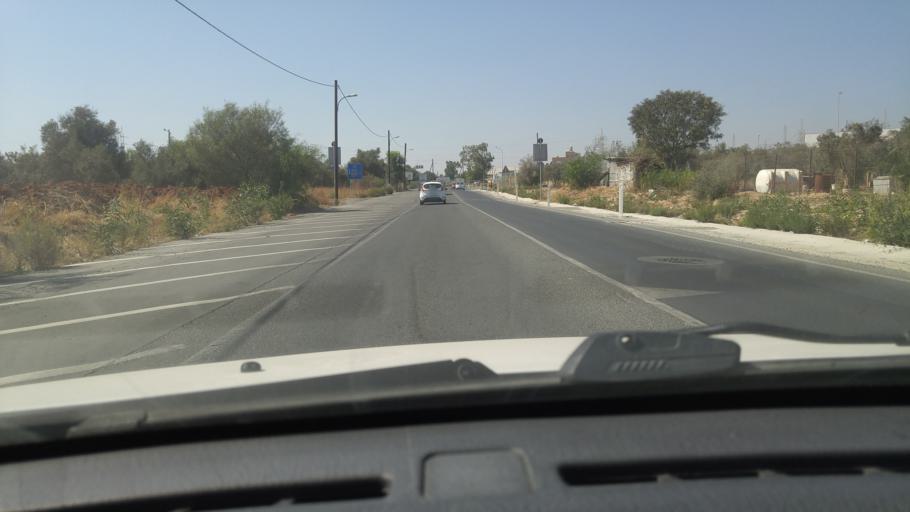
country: CY
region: Limassol
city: Ypsonas
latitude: 34.6807
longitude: 32.9849
